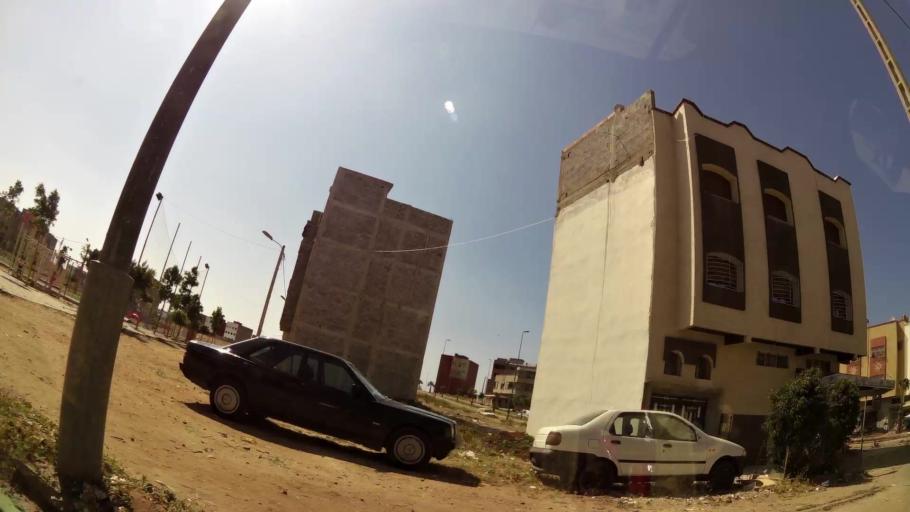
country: MA
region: Rabat-Sale-Zemmour-Zaer
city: Sale
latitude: 34.0720
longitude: -6.7657
